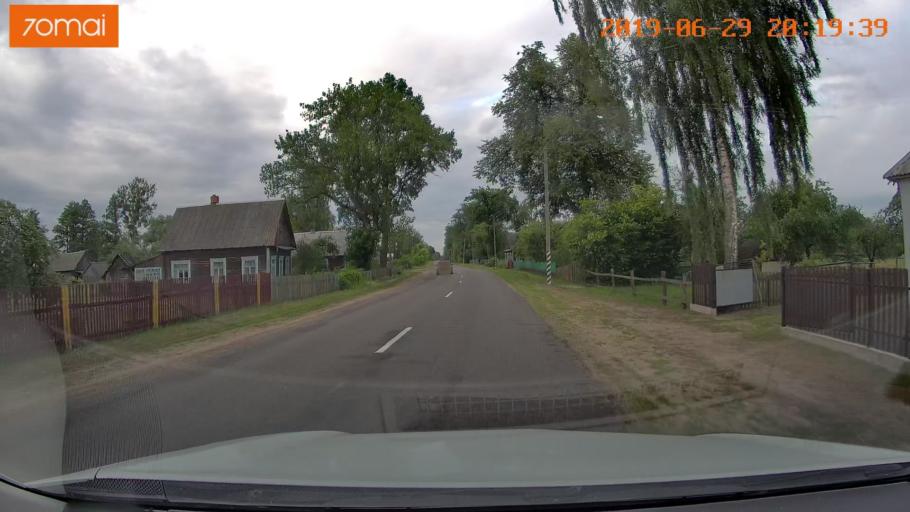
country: BY
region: Brest
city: Asnyezhytsy
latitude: 52.4032
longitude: 26.2454
